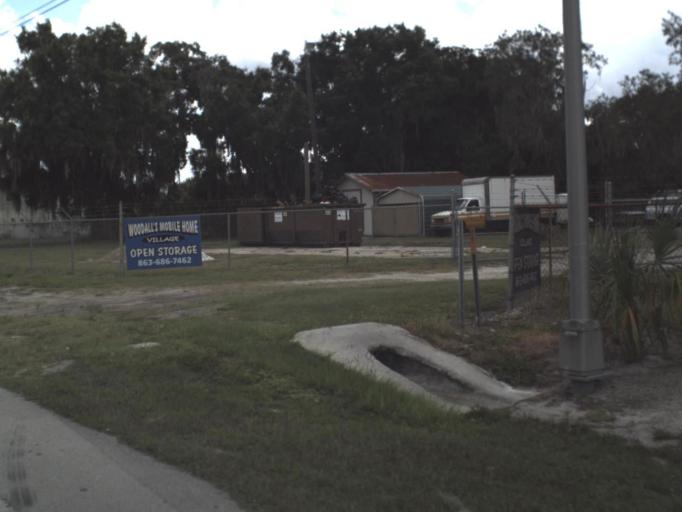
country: US
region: Florida
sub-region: Polk County
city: Winston
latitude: 28.0411
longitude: -81.9926
